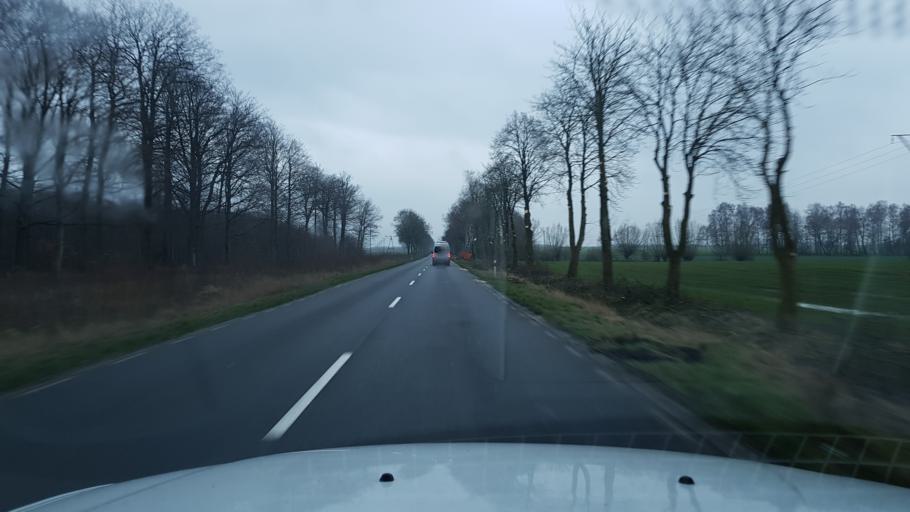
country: PL
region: West Pomeranian Voivodeship
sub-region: Powiat gryficki
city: Gryfice
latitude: 53.8840
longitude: 15.2105
